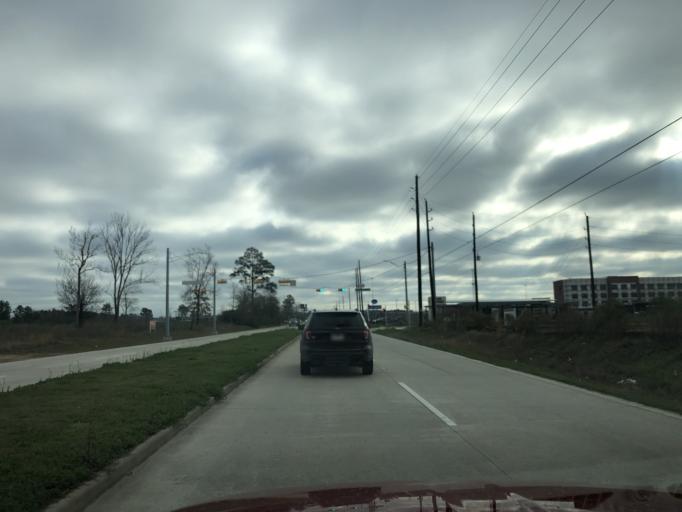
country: US
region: Texas
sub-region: Harris County
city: Spring
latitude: 30.0824
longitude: -95.4453
